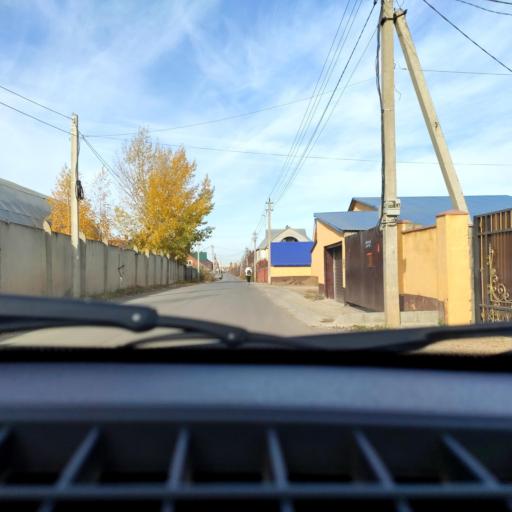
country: RU
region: Bashkortostan
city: Ufa
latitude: 54.6391
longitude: 55.9225
